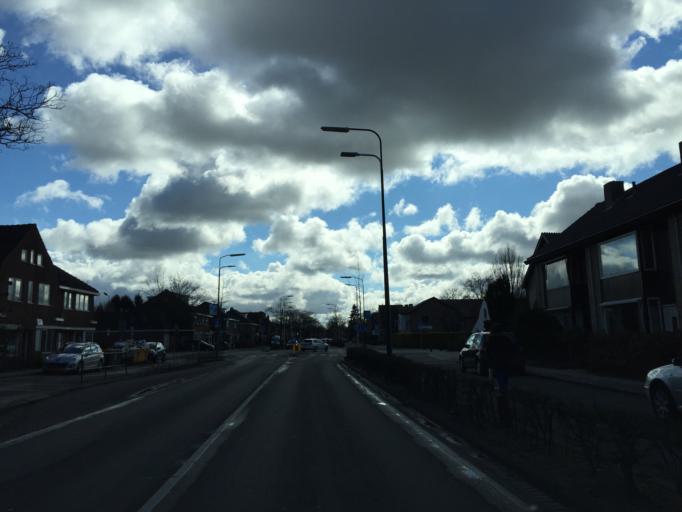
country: NL
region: Utrecht
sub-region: Stichtse Vecht
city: Maarssen
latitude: 52.0810
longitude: 5.0362
